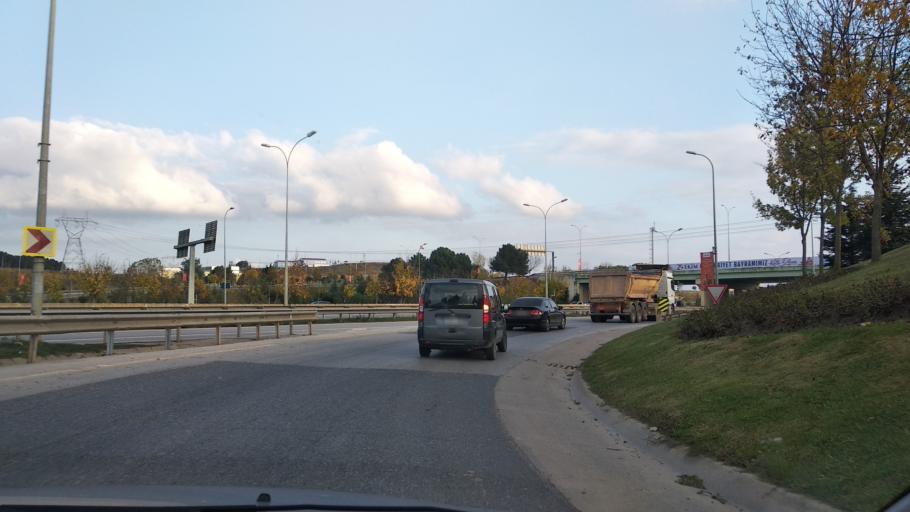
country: TR
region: Istanbul
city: Pendik
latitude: 40.9156
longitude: 29.3233
